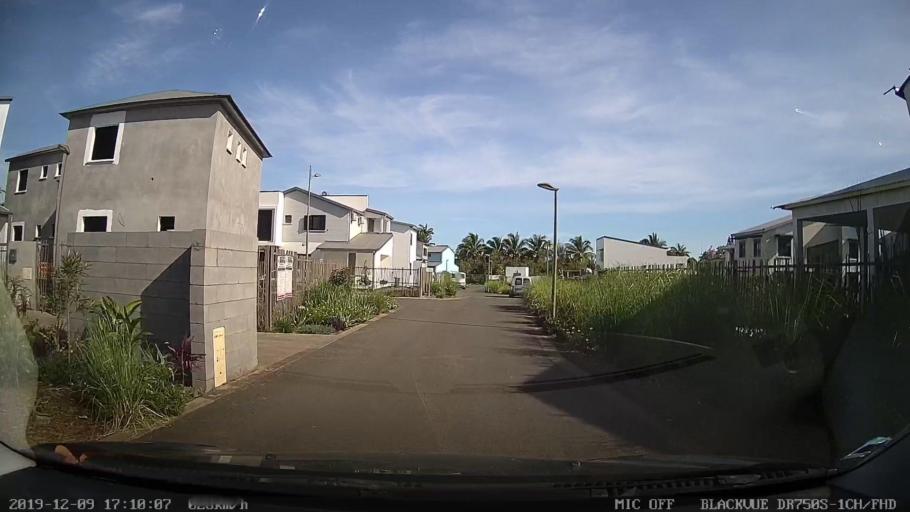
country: RE
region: Reunion
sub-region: Reunion
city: Sainte-Marie
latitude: -20.9087
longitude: 55.5190
